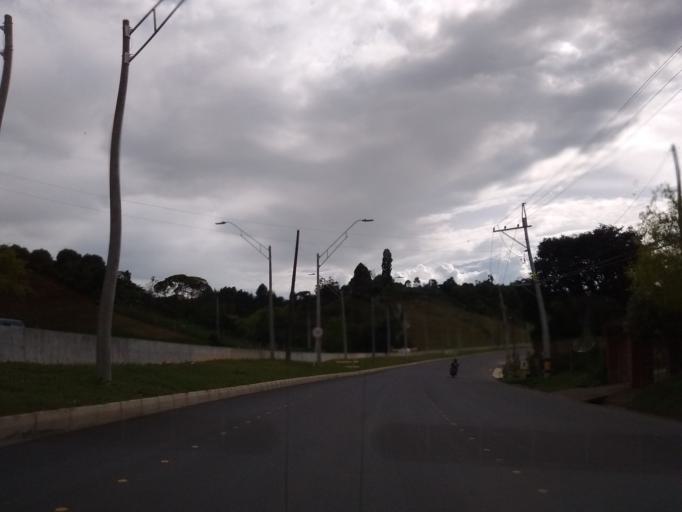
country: CO
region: Antioquia
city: Santuario
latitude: 6.1342
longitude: -75.2884
